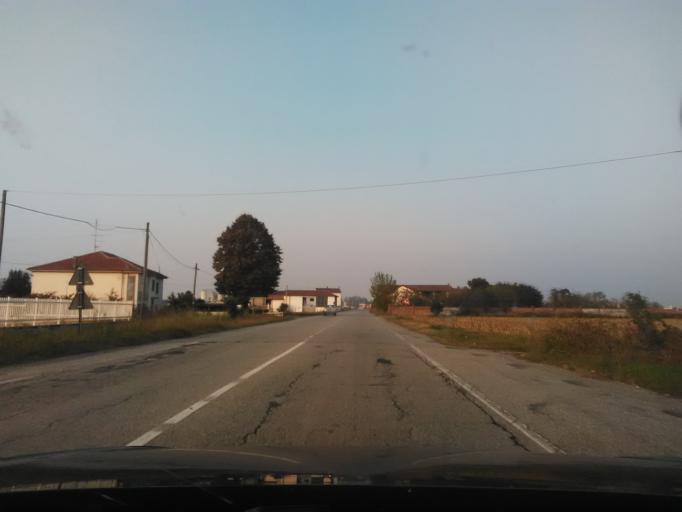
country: IT
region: Piedmont
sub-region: Provincia di Alessandria
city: Casale Monferrato
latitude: 45.1603
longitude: 8.4585
